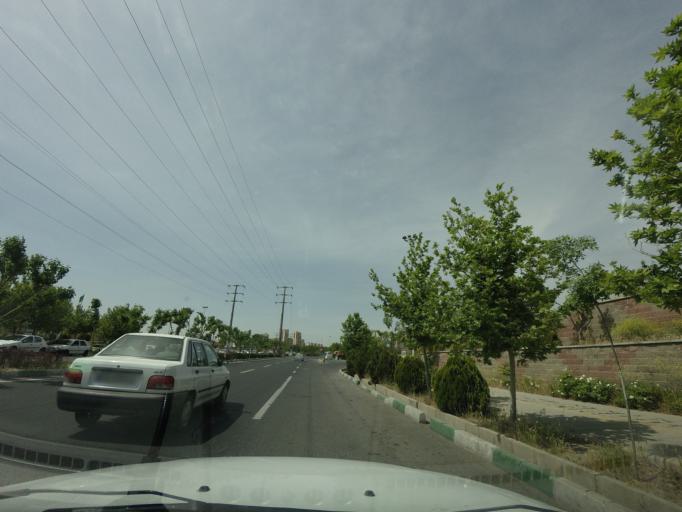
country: IR
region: Tehran
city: Shahr-e Qods
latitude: 35.7517
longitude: 51.2063
